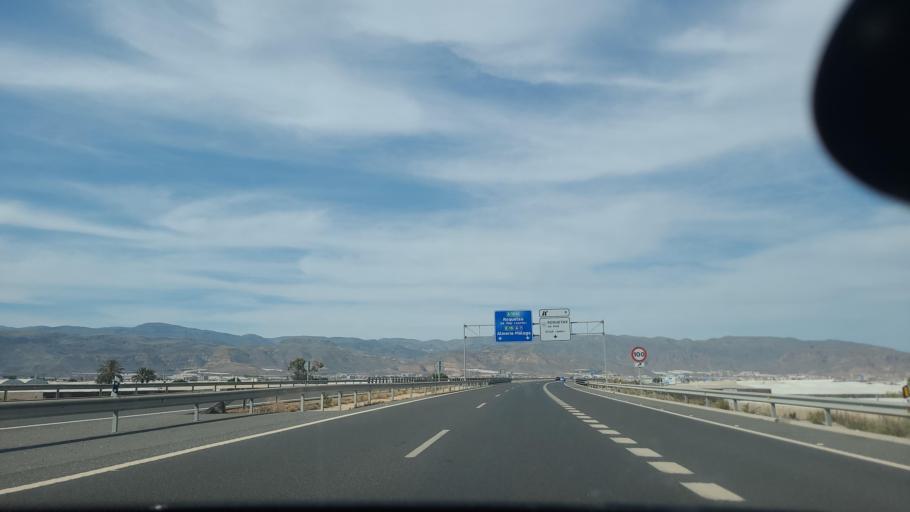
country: ES
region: Andalusia
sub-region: Provincia de Almeria
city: Roquetas de Mar
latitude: 36.7730
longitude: -2.6387
